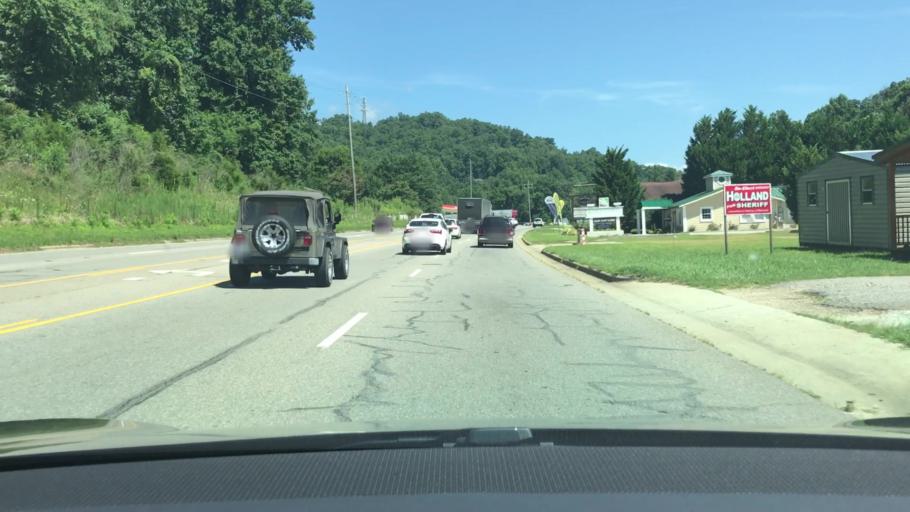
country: US
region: North Carolina
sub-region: Macon County
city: Franklin
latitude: 35.1362
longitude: -83.3979
